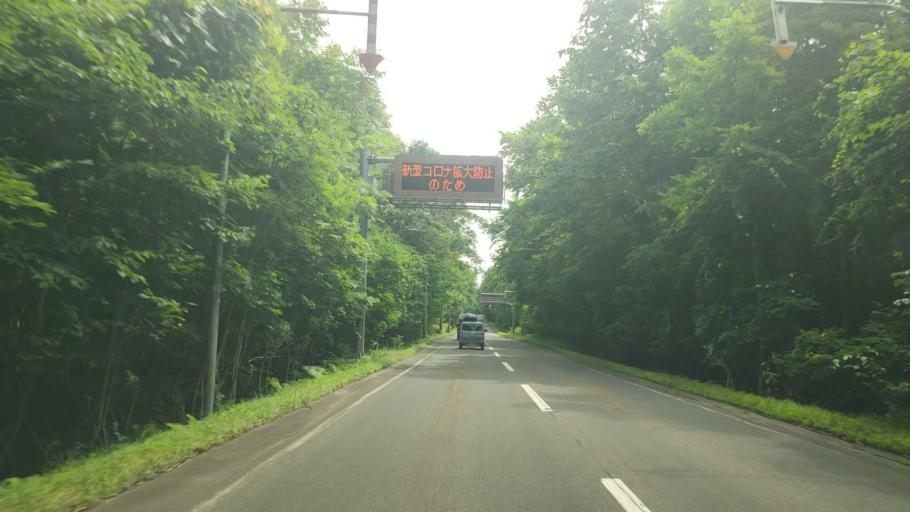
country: JP
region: Hokkaido
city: Tomakomai
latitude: 42.7706
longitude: 141.4397
